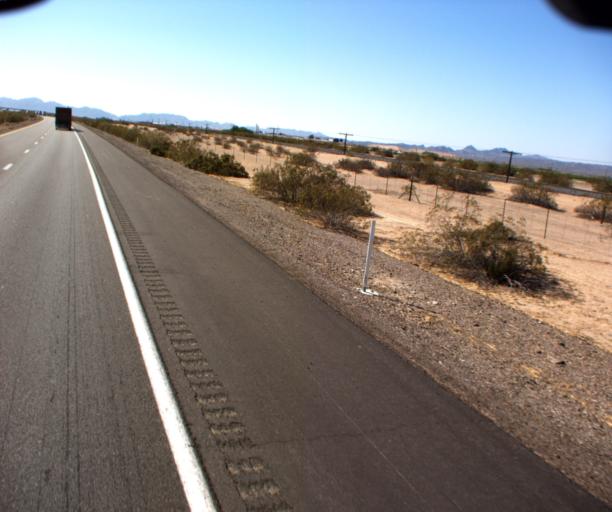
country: US
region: Arizona
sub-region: Yuma County
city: Wellton
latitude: 32.6729
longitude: -114.0935
